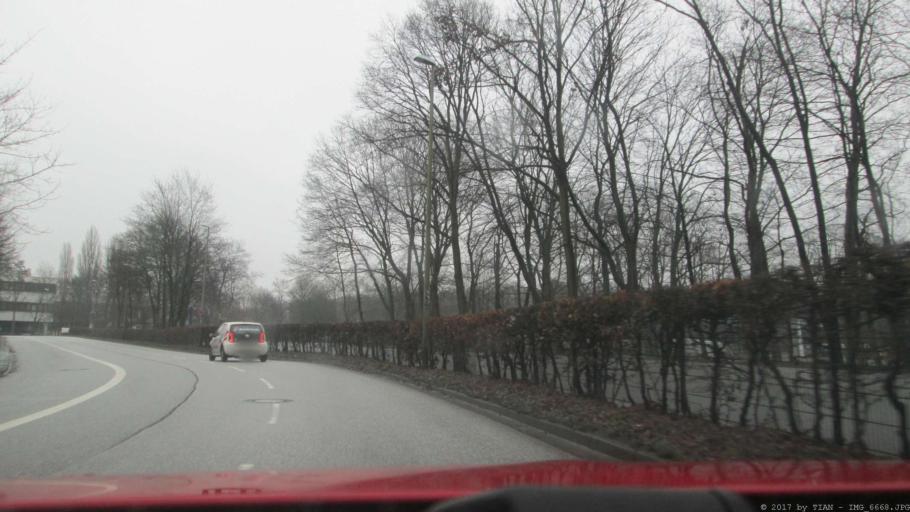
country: DE
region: Hamburg
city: Eidelstedt
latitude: 53.5883
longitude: 9.9011
